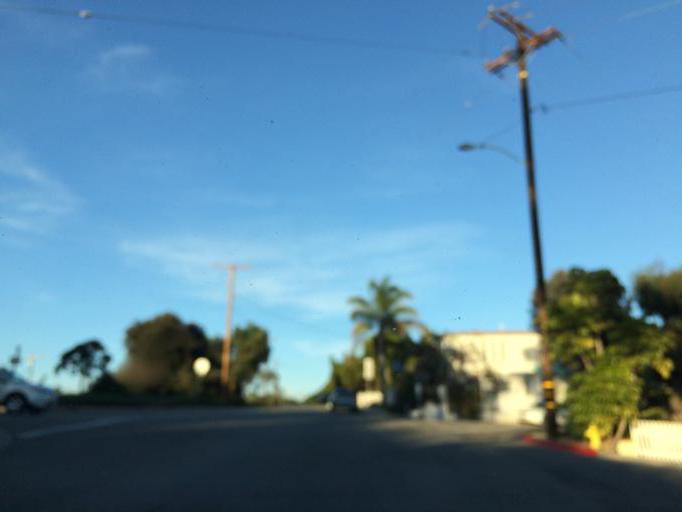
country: US
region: California
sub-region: Los Angeles County
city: Manhattan Beach
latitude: 33.8956
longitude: -118.4007
